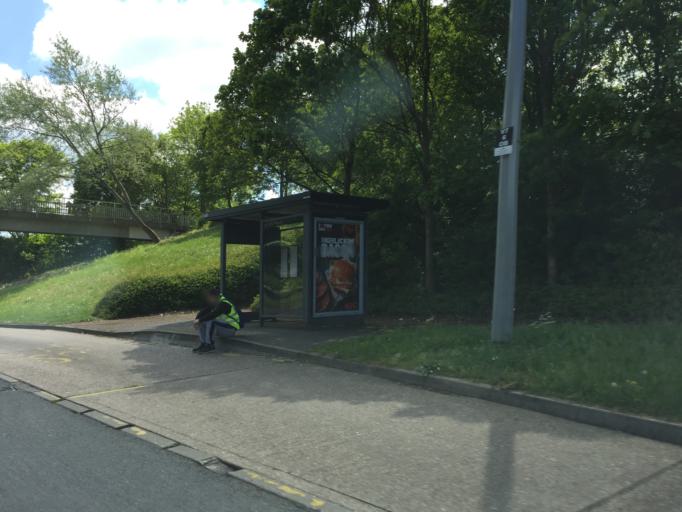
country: GB
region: England
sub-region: Milton Keynes
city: Milton Keynes
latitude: 52.0322
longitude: -0.7468
